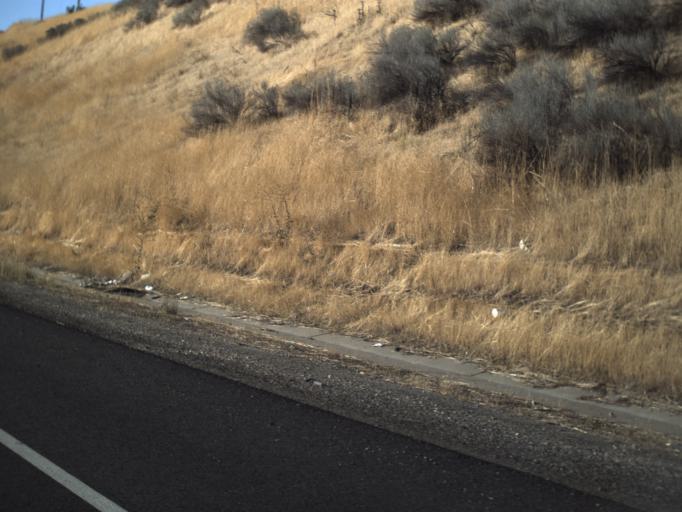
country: US
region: Utah
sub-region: Weber County
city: South Ogden
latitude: 41.2038
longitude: -111.9964
